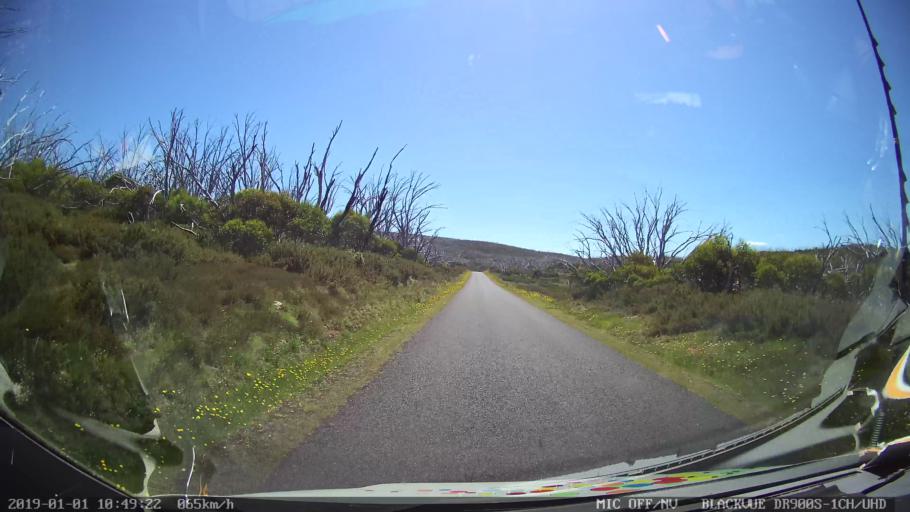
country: AU
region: New South Wales
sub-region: Snowy River
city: Jindabyne
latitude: -36.0350
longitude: 148.3696
